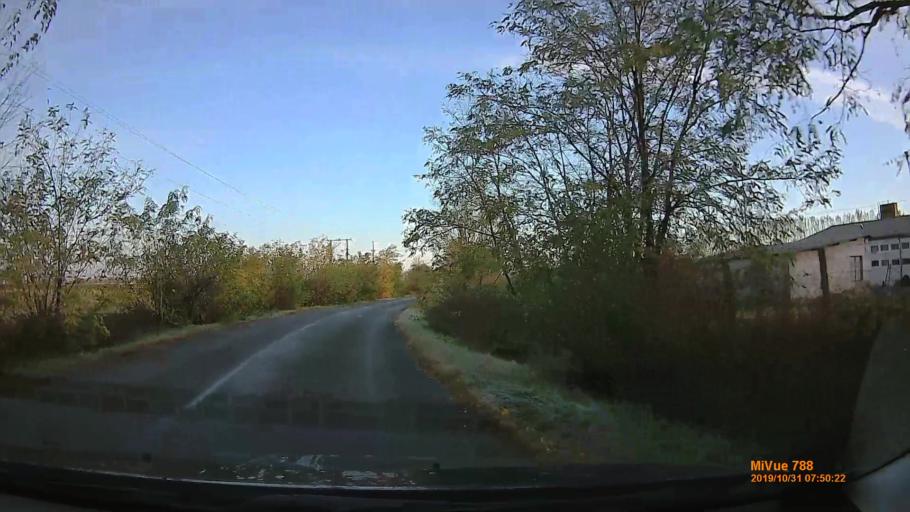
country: HU
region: Pest
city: Pilis
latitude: 47.3023
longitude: 19.5615
